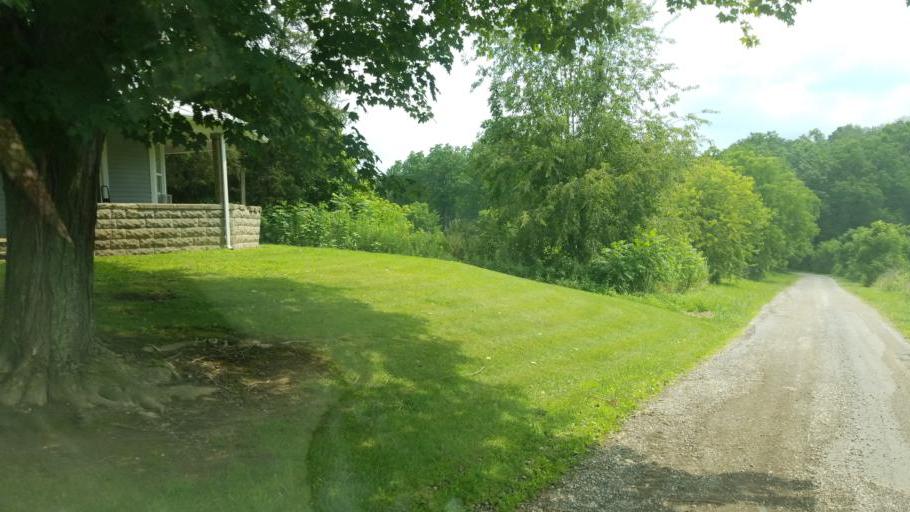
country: US
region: Ohio
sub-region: Licking County
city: Utica
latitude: 40.2048
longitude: -82.4970
